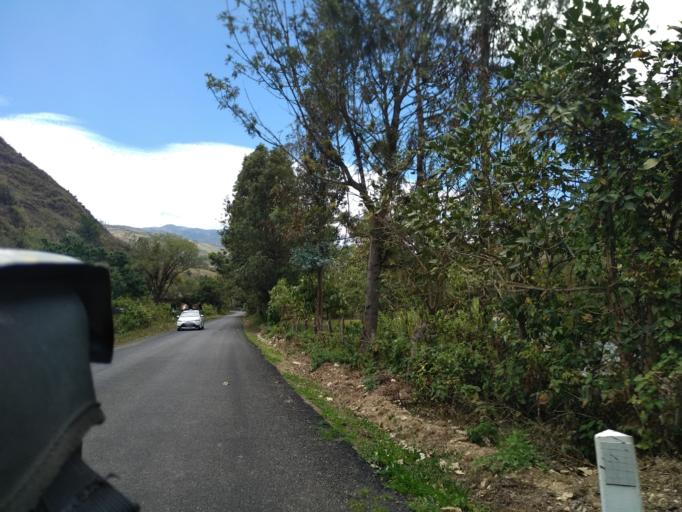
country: PE
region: Amazonas
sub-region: Provincia de Chachapoyas
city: Montevideo
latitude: -6.6347
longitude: -77.8133
